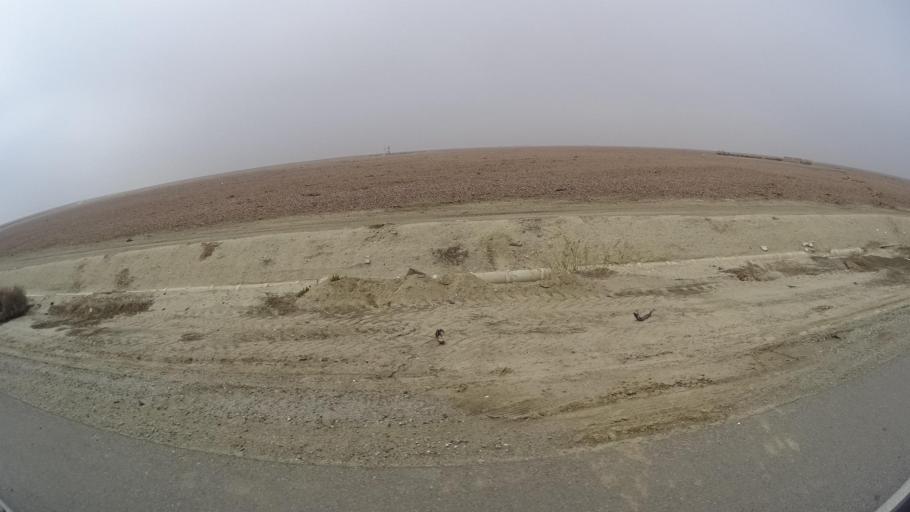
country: US
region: California
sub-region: Kern County
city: Greenfield
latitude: 35.0791
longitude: -119.1241
